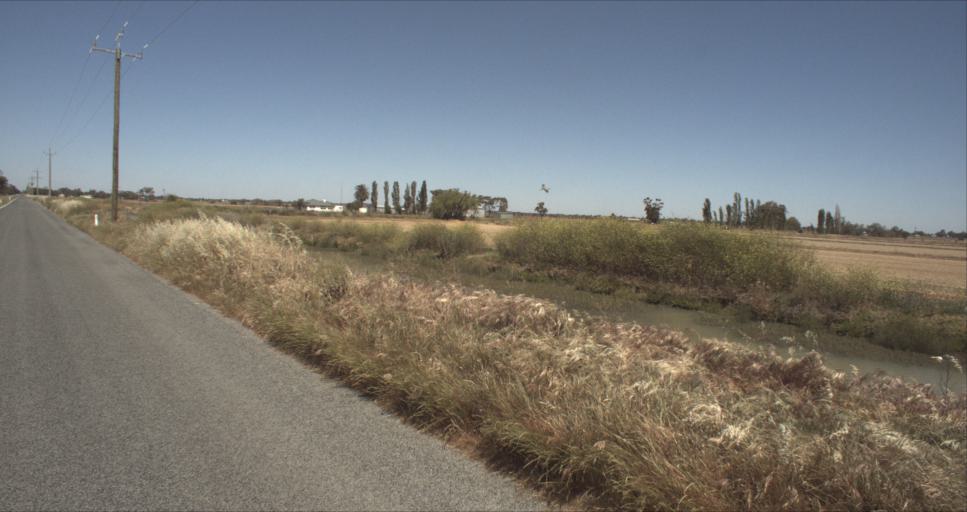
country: AU
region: New South Wales
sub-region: Leeton
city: Leeton
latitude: -34.5104
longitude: 146.4269
